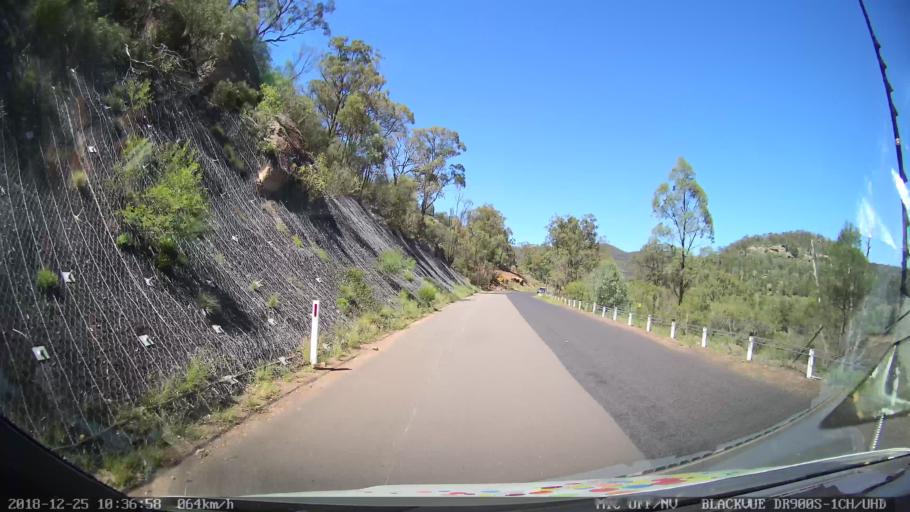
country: AU
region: New South Wales
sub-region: Upper Hunter Shire
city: Merriwa
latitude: -32.4092
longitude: 150.3825
